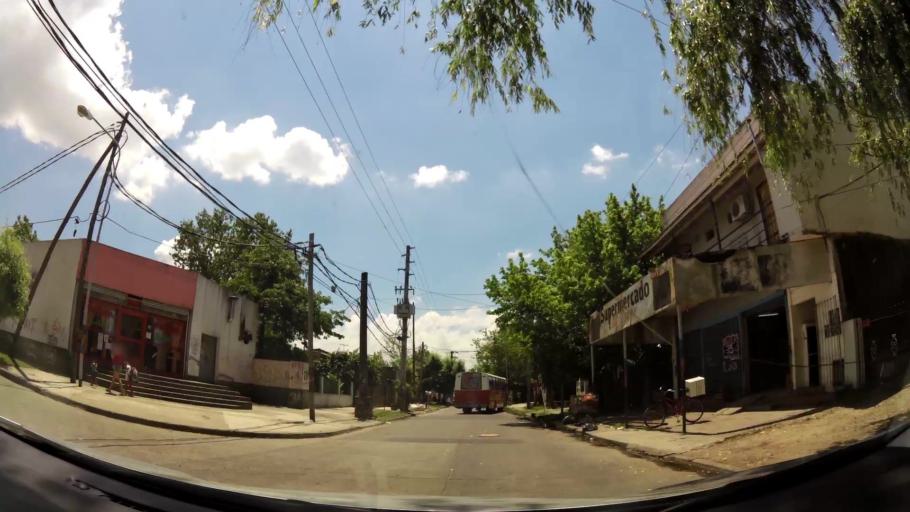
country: AR
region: Buenos Aires
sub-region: Partido de Tigre
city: Tigre
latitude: -34.4090
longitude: -58.5998
